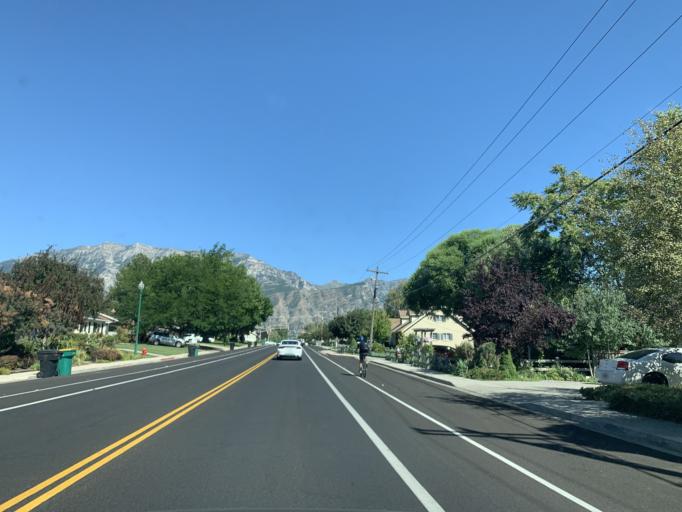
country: US
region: Utah
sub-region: Utah County
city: Orem
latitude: 40.2826
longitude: -111.7075
